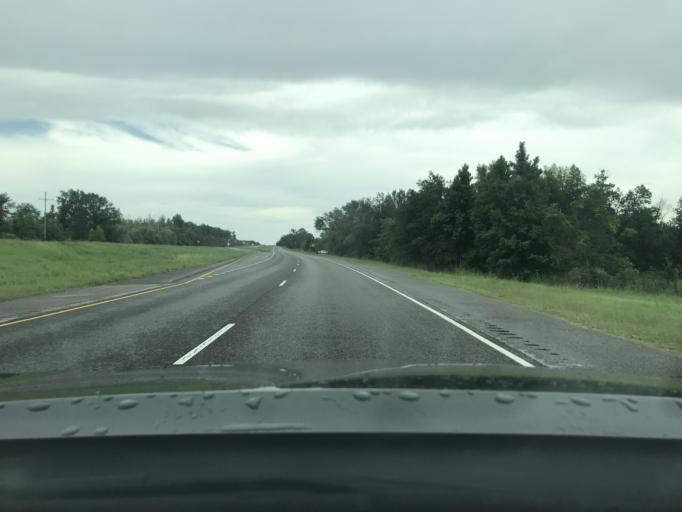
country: US
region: Louisiana
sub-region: Calcasieu Parish
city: Moss Bluff
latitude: 30.3967
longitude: -93.2306
